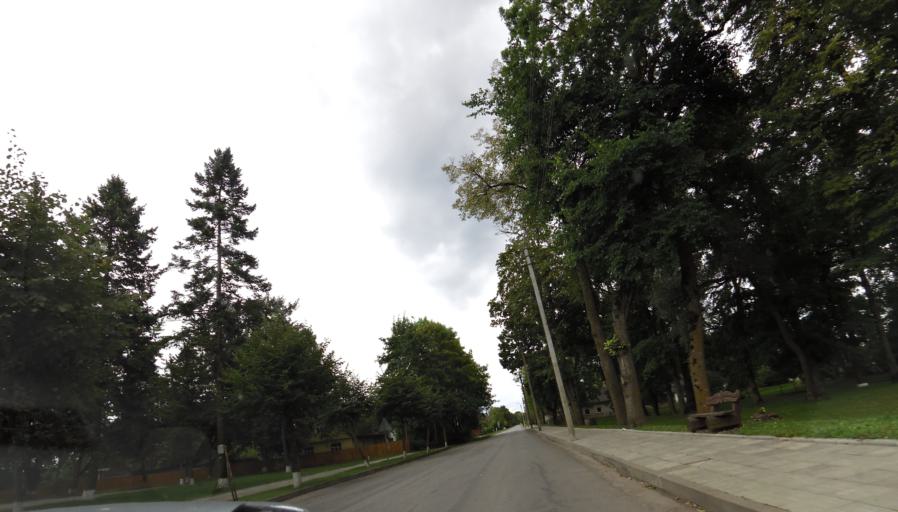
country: LT
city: Linkuva
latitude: 56.0205
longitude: 24.1677
